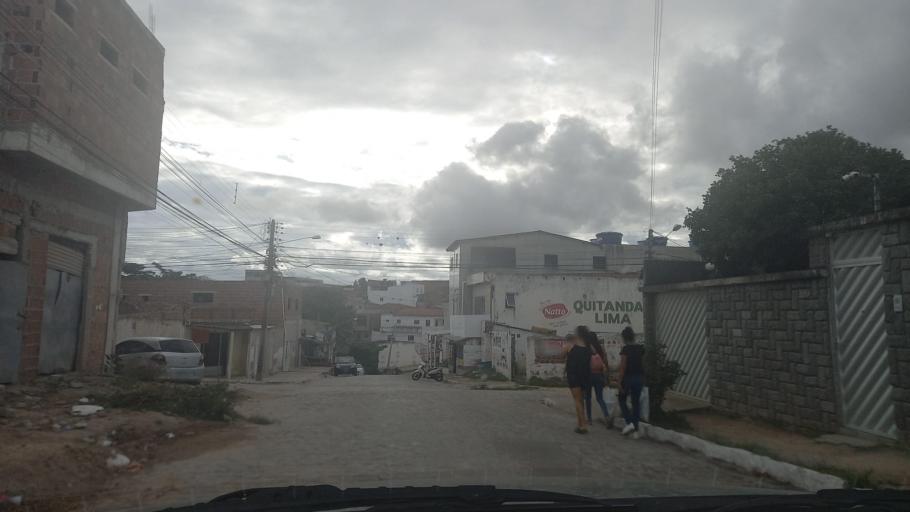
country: BR
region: Pernambuco
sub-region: Caruaru
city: Caruaru
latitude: -8.2969
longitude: -35.9842
